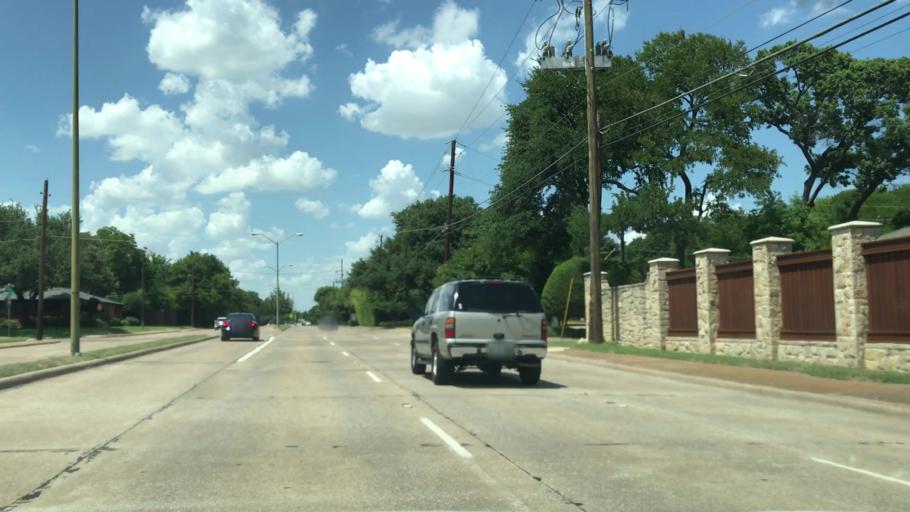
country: US
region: Texas
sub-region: Dallas County
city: University Park
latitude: 32.8735
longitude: -96.8385
